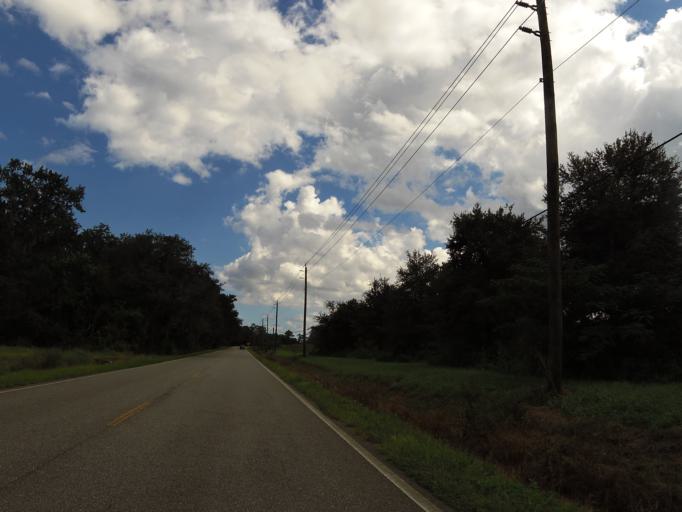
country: US
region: Florida
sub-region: Saint Johns County
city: Saint Augustine South
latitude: 29.8222
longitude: -81.4887
